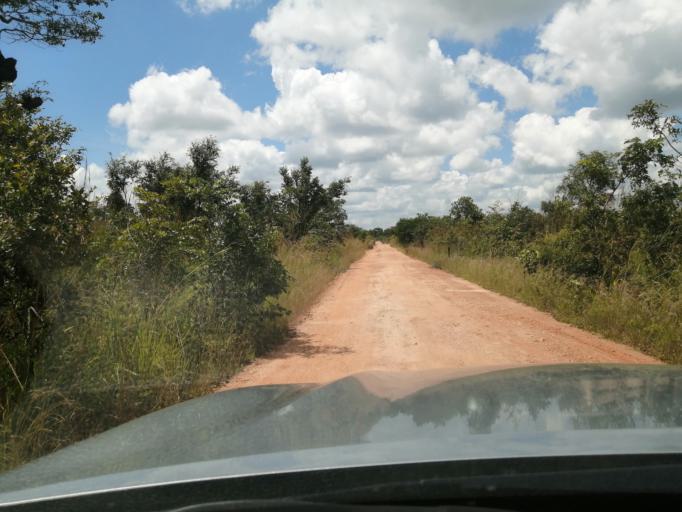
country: ZM
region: Lusaka
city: Lusaka
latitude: -15.1502
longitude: 27.9415
